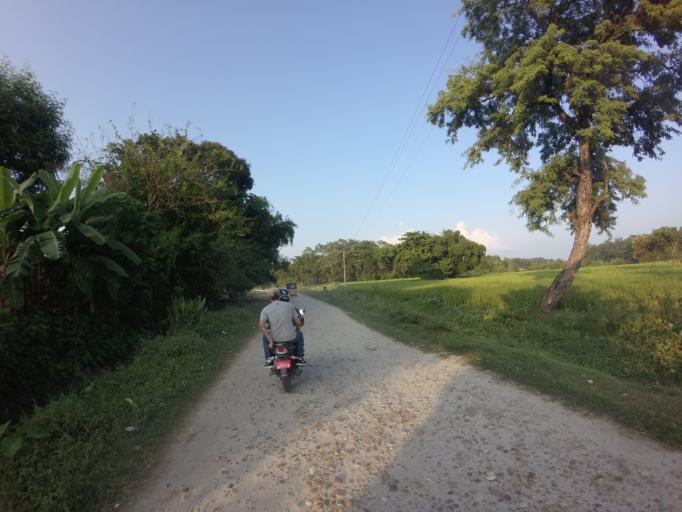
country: NP
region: Far Western
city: Tikapur
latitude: 28.4530
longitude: 81.0725
